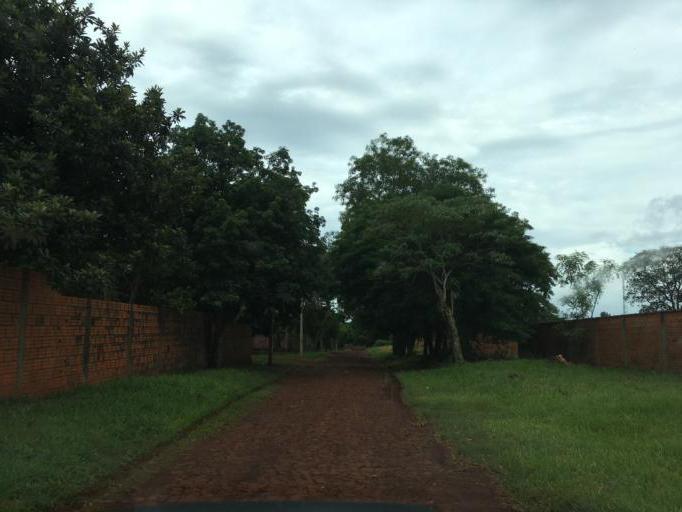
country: PY
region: Alto Parana
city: Ciudad del Este
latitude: -25.4237
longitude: -54.6432
